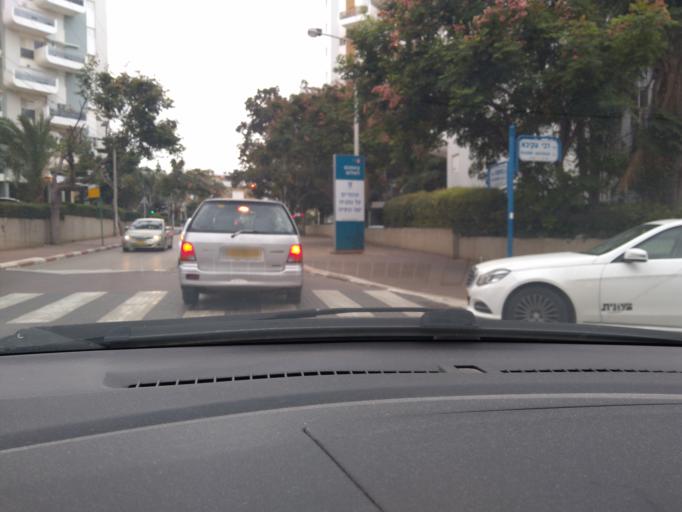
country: IL
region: Central District
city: Netanya
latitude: 32.3428
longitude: 34.8621
